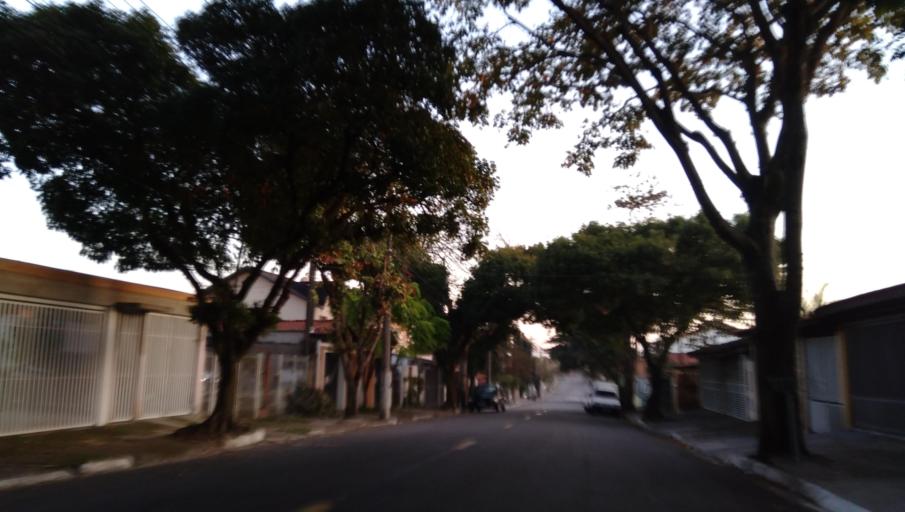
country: BR
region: Sao Paulo
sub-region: Sao Jose Dos Campos
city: Sao Jose dos Campos
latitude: -23.1782
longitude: -45.8206
